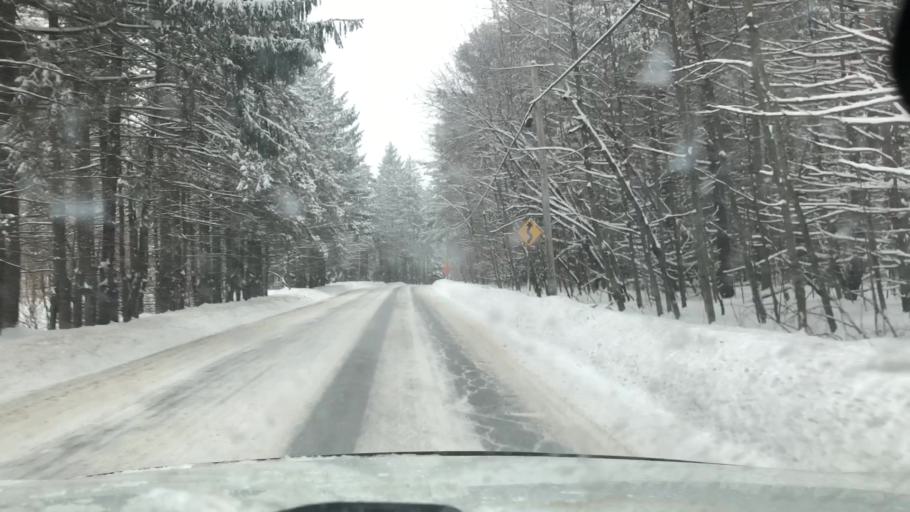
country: CA
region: Quebec
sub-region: Outaouais
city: Gatineau
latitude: 45.5138
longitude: -75.8383
